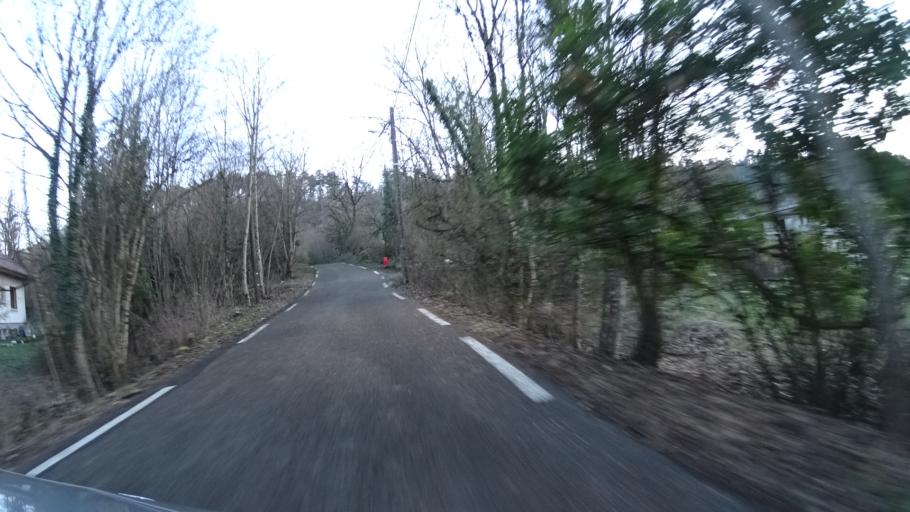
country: FR
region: Franche-Comte
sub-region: Departement du Doubs
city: Morre
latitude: 47.2198
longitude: 6.0414
